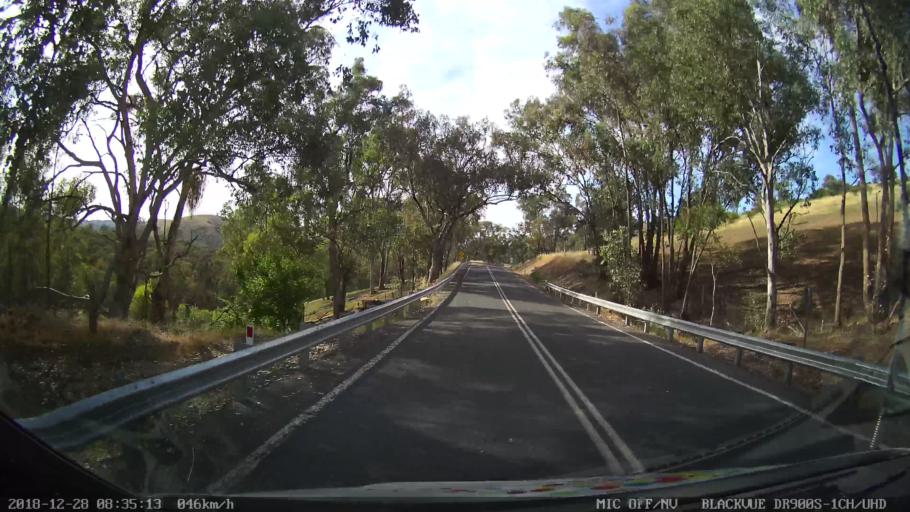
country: AU
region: New South Wales
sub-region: Blayney
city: Blayney
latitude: -33.9817
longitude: 149.3096
